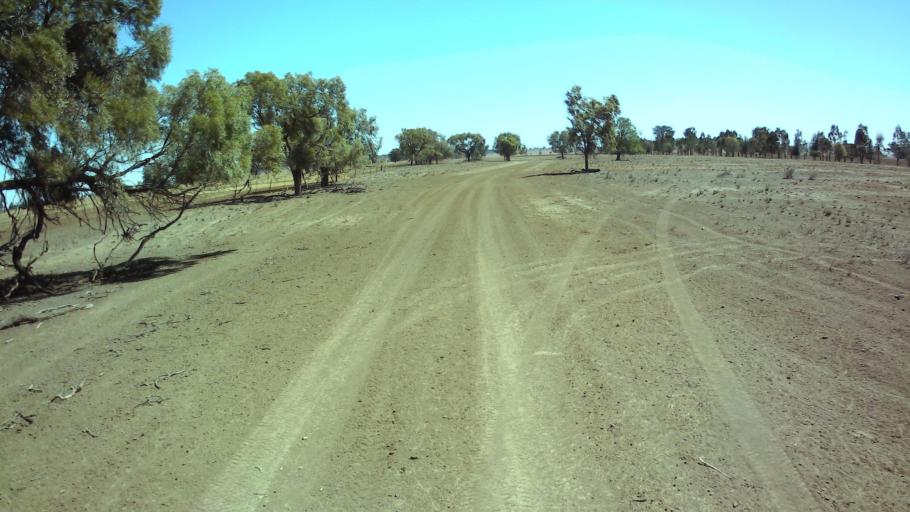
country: AU
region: New South Wales
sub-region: Forbes
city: Forbes
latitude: -33.7172
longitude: 147.6664
